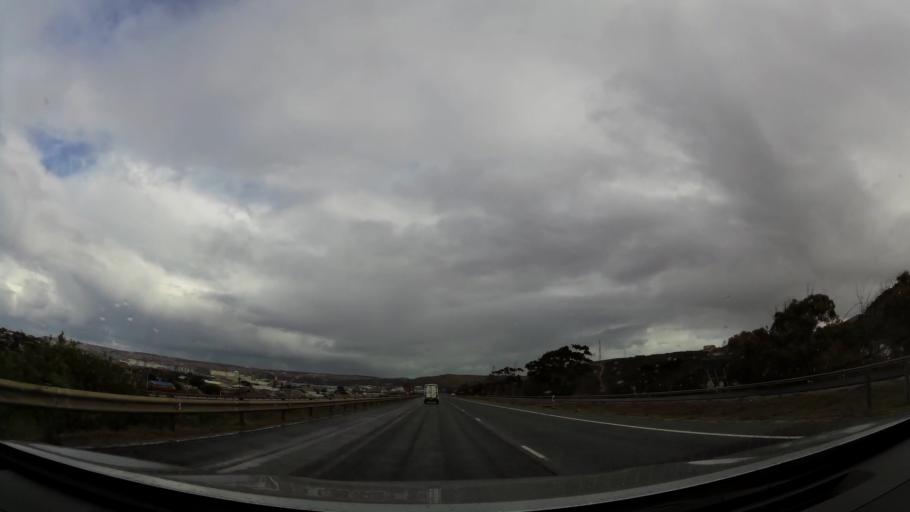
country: ZA
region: Western Cape
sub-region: Eden District Municipality
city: Mossel Bay
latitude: -34.1357
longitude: 22.1016
